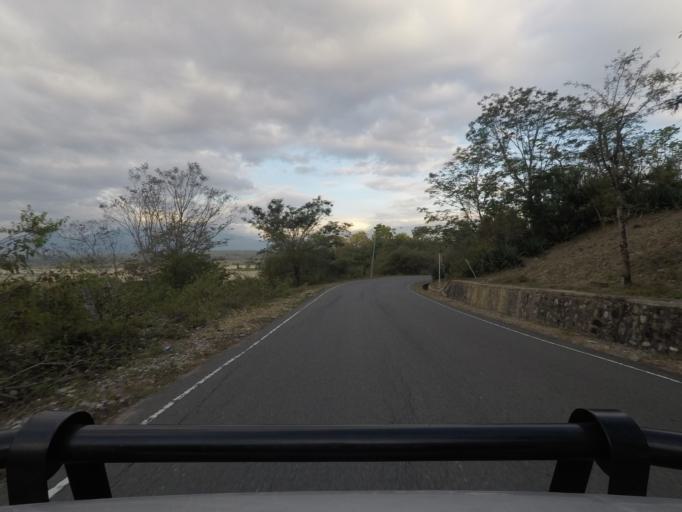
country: TL
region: Bobonaro
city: Maliana
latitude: -8.9514
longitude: 125.1077
